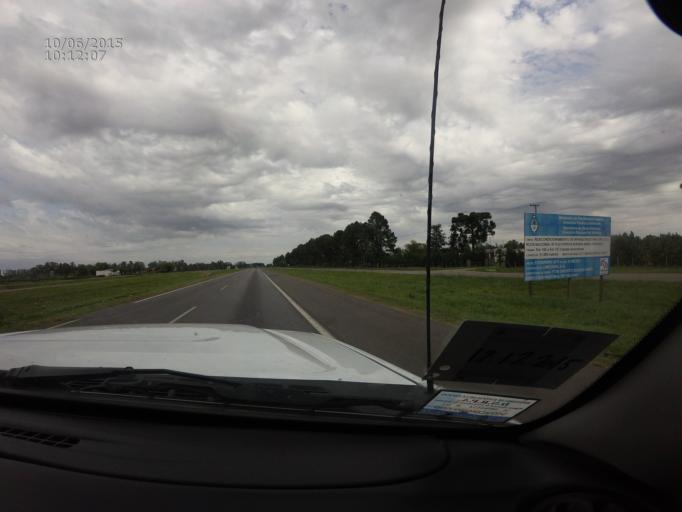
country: AR
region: Buenos Aires
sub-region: Partido de San Pedro
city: San Pedro
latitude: -33.7739
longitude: -59.6681
